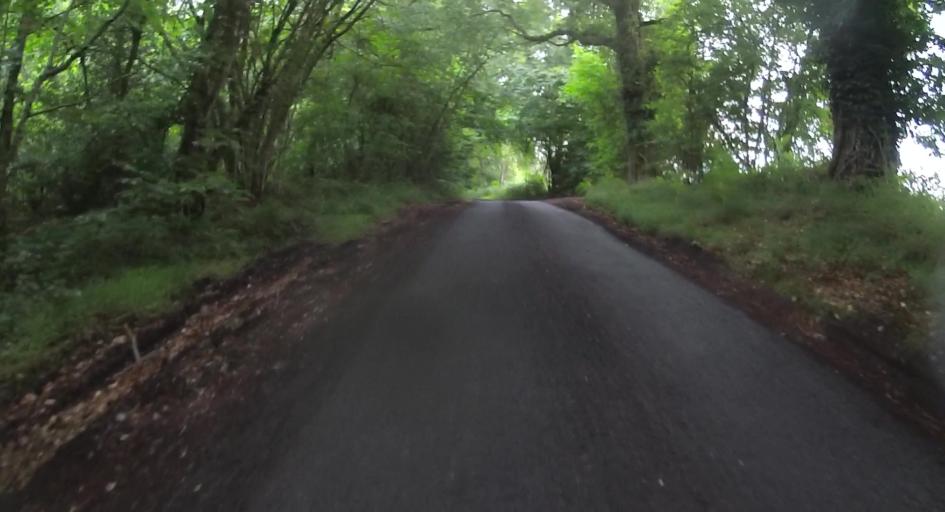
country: GB
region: England
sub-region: Hampshire
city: Long Sutton
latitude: 51.2055
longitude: -0.9160
